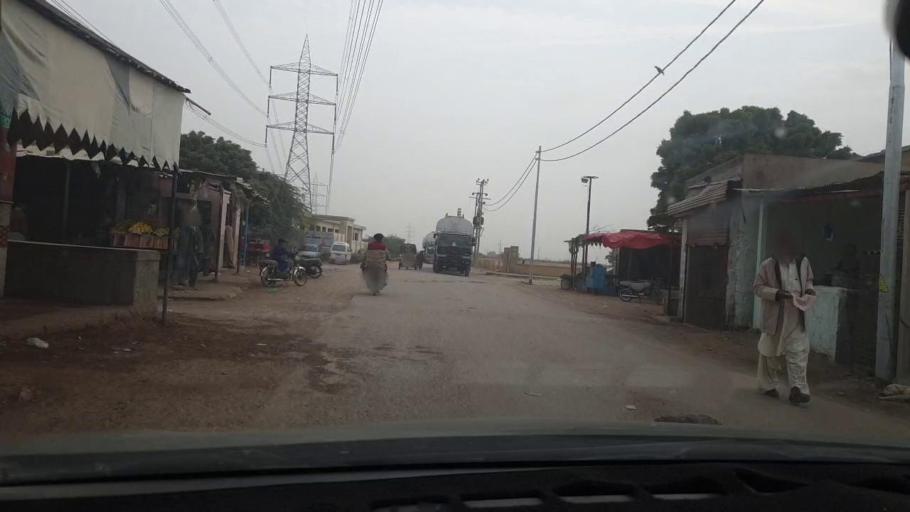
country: PK
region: Sindh
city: Malir Cantonment
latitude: 24.9064
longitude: 67.2863
